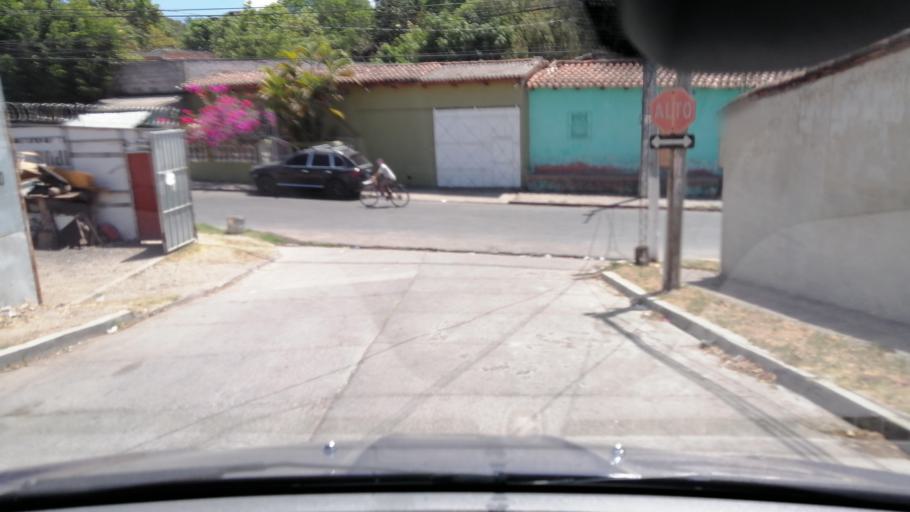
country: SV
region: Santa Ana
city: Metapan
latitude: 14.3326
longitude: -89.4402
